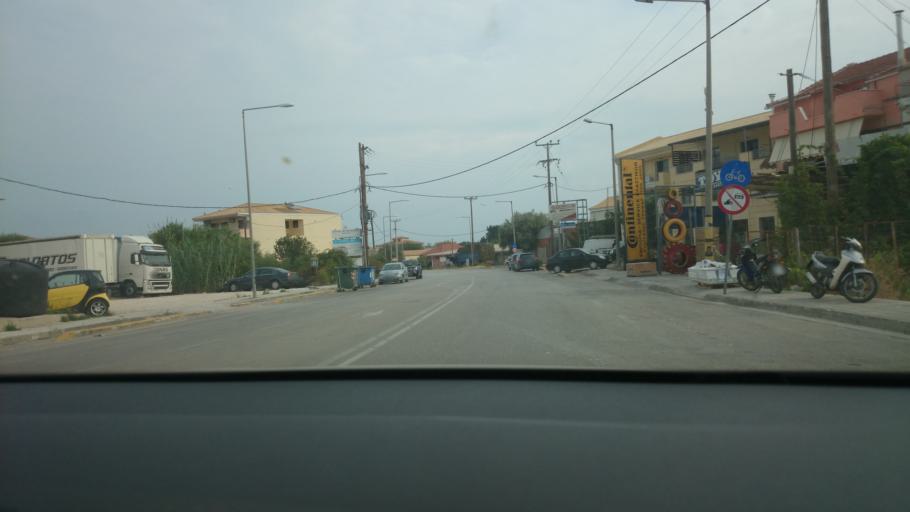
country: GR
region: Ionian Islands
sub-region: Lefkada
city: Lefkada
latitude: 38.8246
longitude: 20.7028
